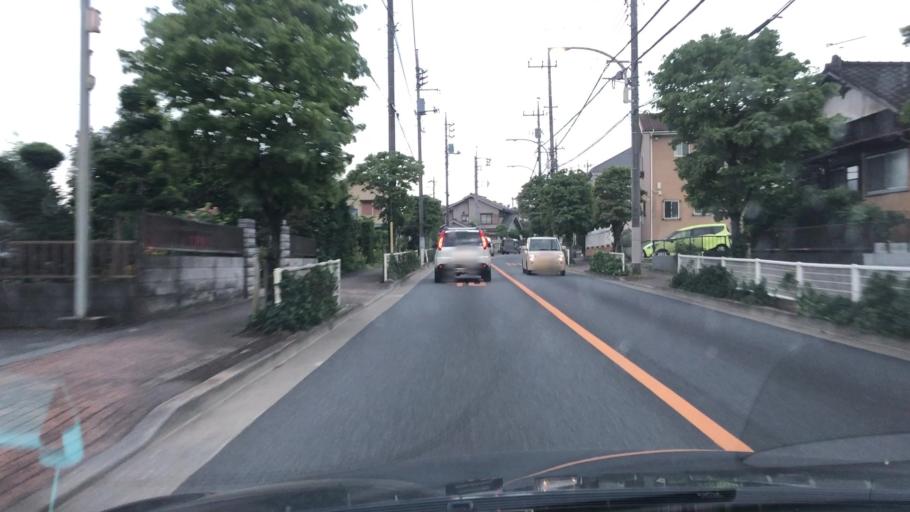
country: JP
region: Tokyo
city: Ome
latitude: 35.7985
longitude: 139.2128
